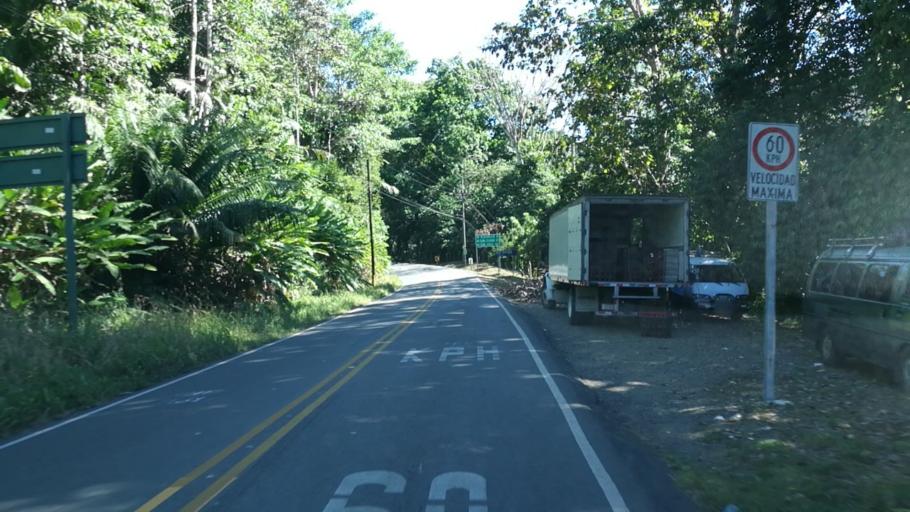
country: CR
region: San Jose
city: San Isidro
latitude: 9.2599
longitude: -83.8638
